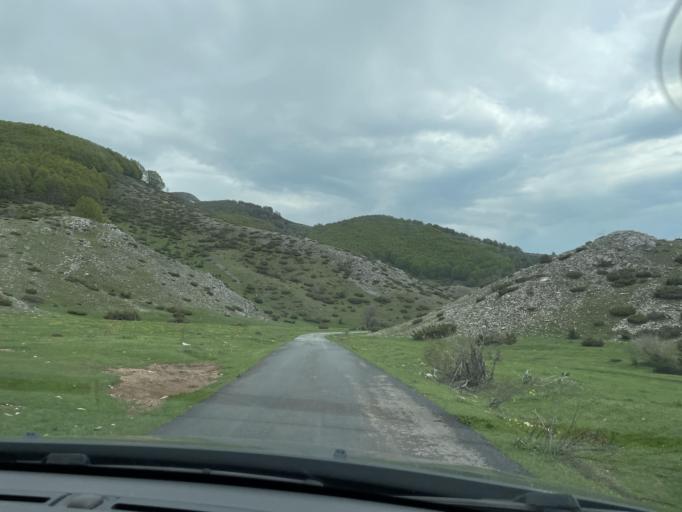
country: MK
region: Opstina Rostusa
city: Rostusha
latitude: 41.6045
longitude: 20.6847
